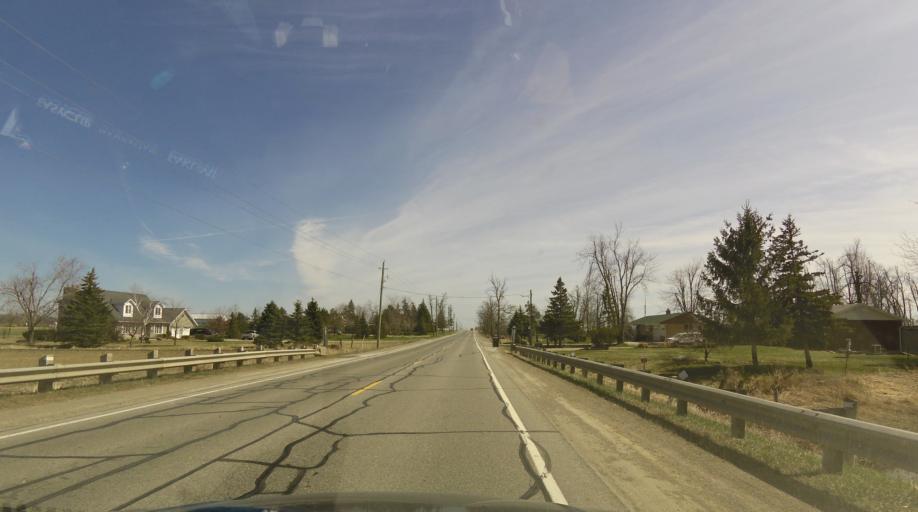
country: CA
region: Ontario
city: Brampton
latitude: 43.6992
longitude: -79.8734
